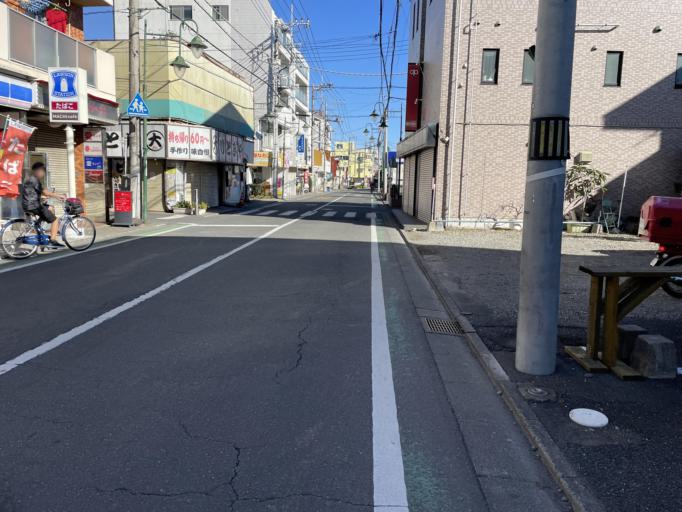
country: JP
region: Saitama
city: Sakado
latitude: 35.9361
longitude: 139.4206
